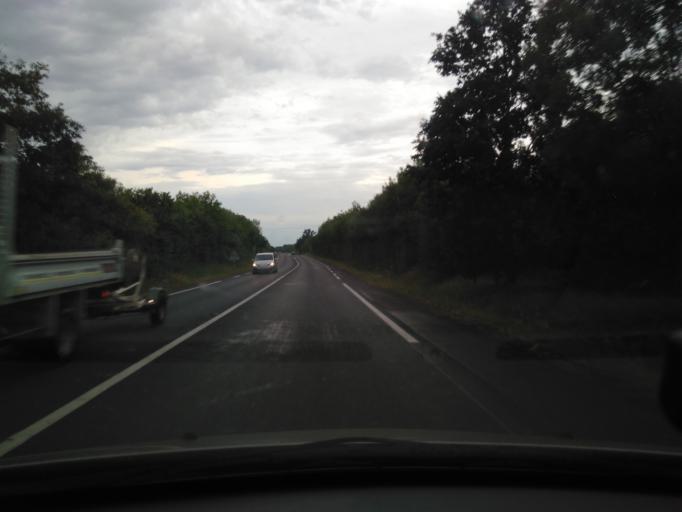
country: FR
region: Pays de la Loire
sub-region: Departement de la Vendee
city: Dompierre-sur-Yon
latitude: 46.7404
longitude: -1.4073
